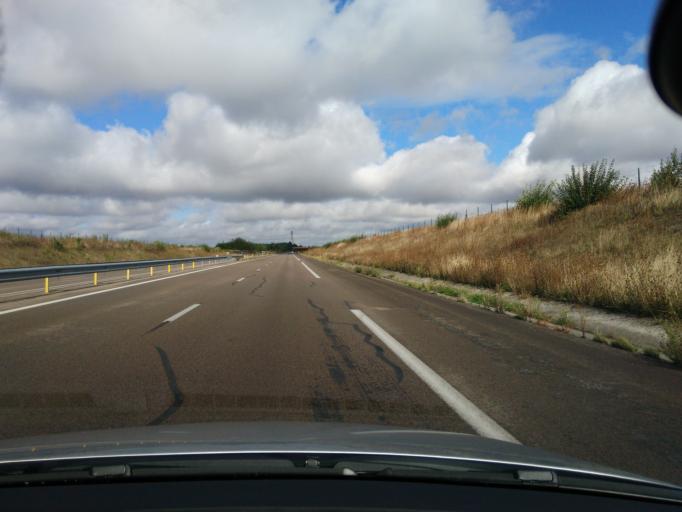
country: FR
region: Haute-Normandie
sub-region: Departement de l'Eure
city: La Madeleine-de-Nonancourt
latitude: 48.8291
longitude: 1.1870
